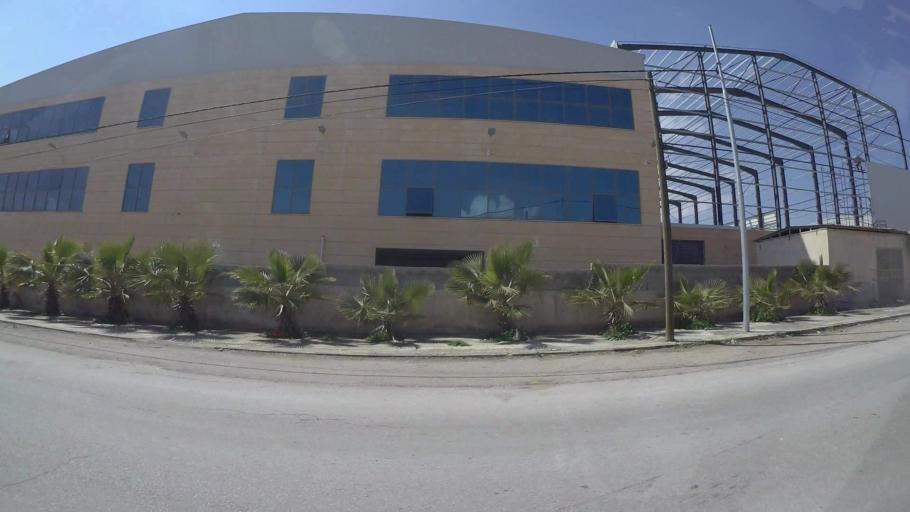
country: JO
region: Zarqa
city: Russeifa
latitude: 31.9951
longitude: 36.0112
